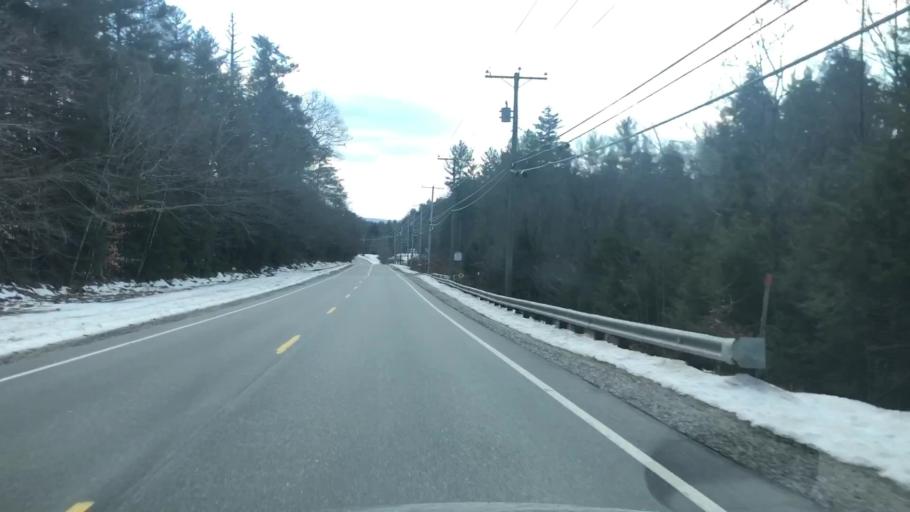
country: US
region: New Hampshire
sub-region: Hillsborough County
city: Mont Vernon
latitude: 42.8670
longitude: -71.6691
